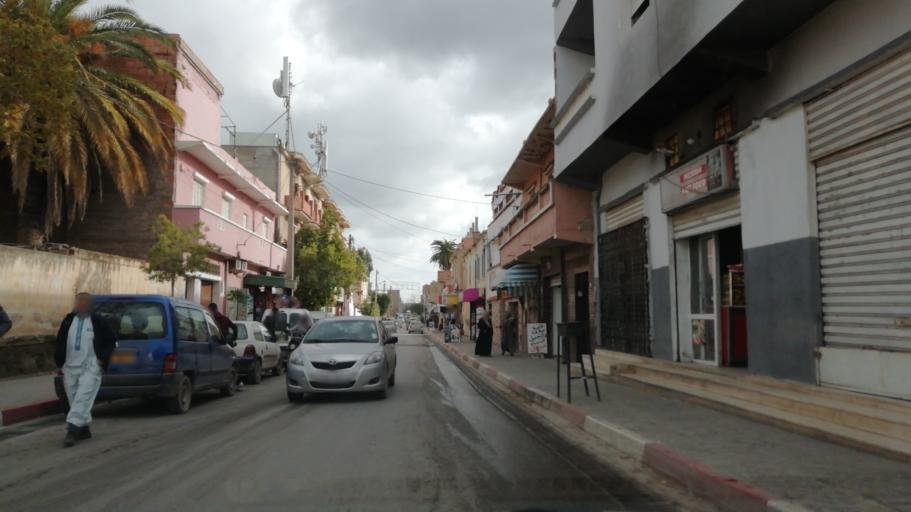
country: DZ
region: Oran
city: Sidi ech Chahmi
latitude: 35.6566
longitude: -0.5232
